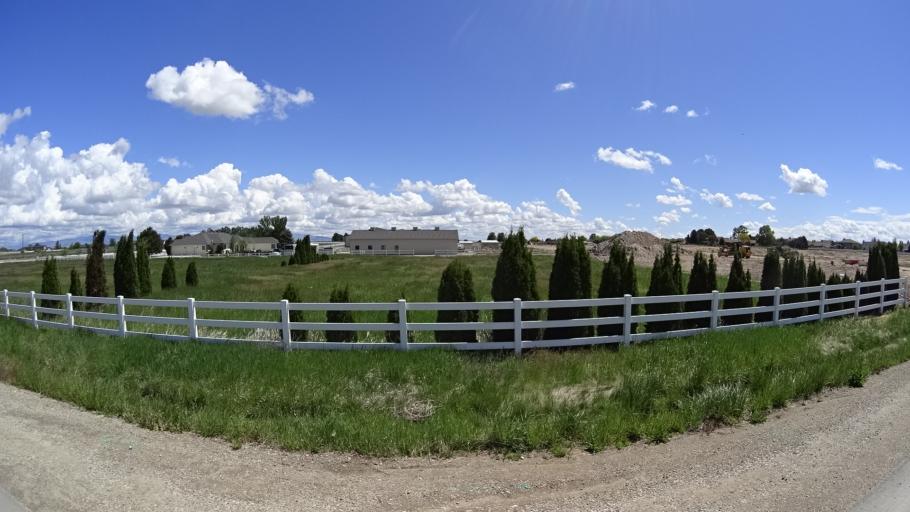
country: US
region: Idaho
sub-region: Ada County
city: Kuna
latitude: 43.5160
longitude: -116.4337
